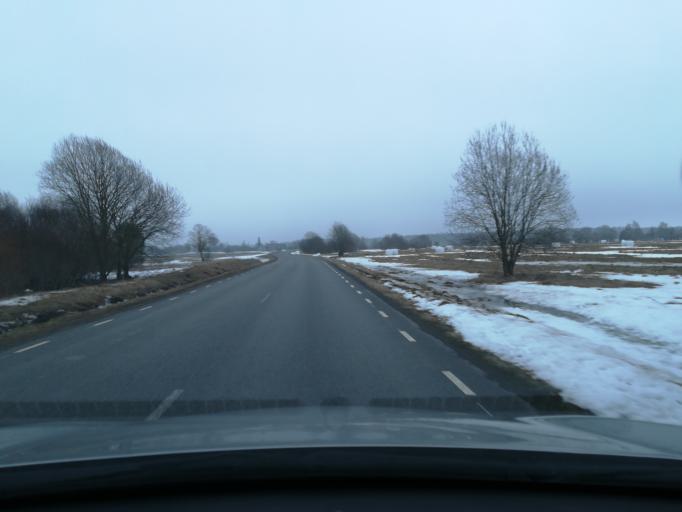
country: EE
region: Harju
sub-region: Kuusalu vald
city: Kuusalu
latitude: 59.4732
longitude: 25.5499
